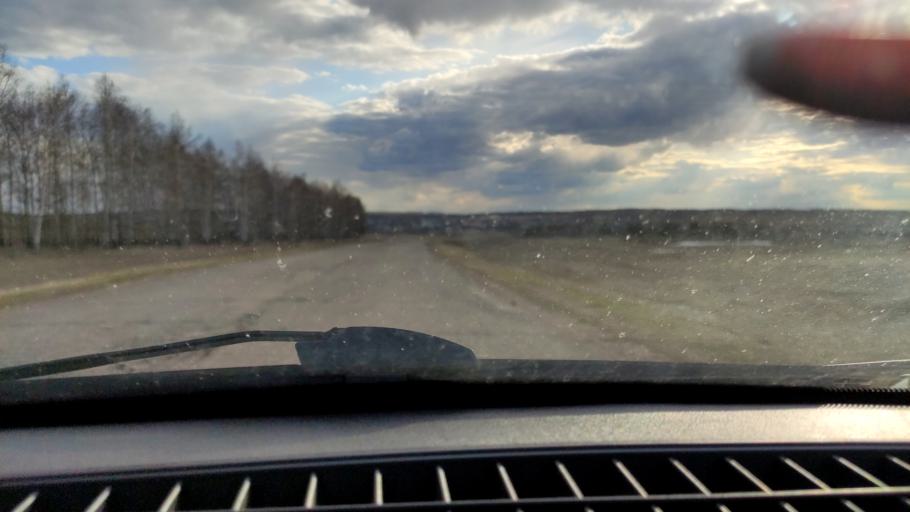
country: RU
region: Bashkortostan
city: Karmaskaly
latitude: 54.3419
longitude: 56.0174
